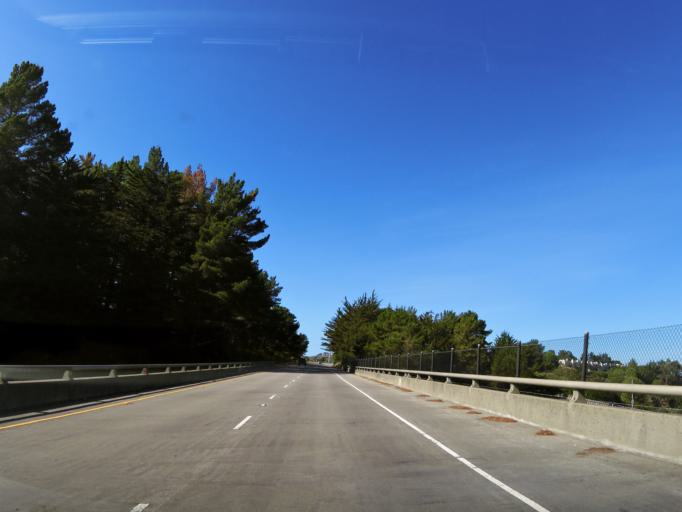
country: US
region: California
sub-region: San Mateo County
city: San Bruno
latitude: 37.6043
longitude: -122.4275
